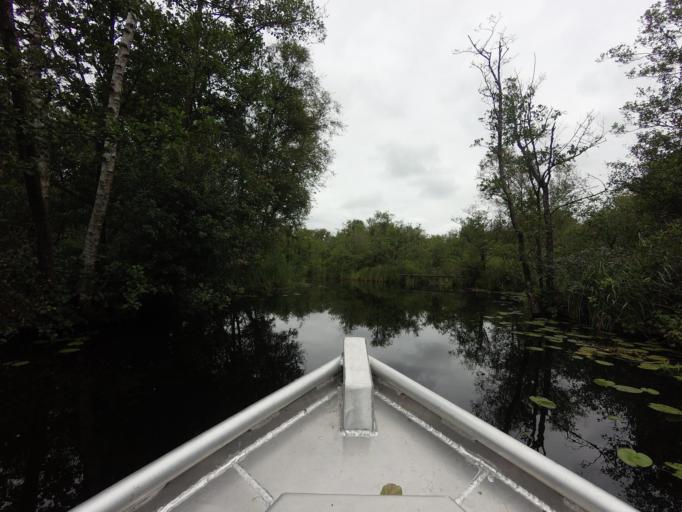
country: NL
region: Overijssel
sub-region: Gemeente Steenwijkerland
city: Oldemarkt
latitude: 52.7886
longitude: 5.9604
